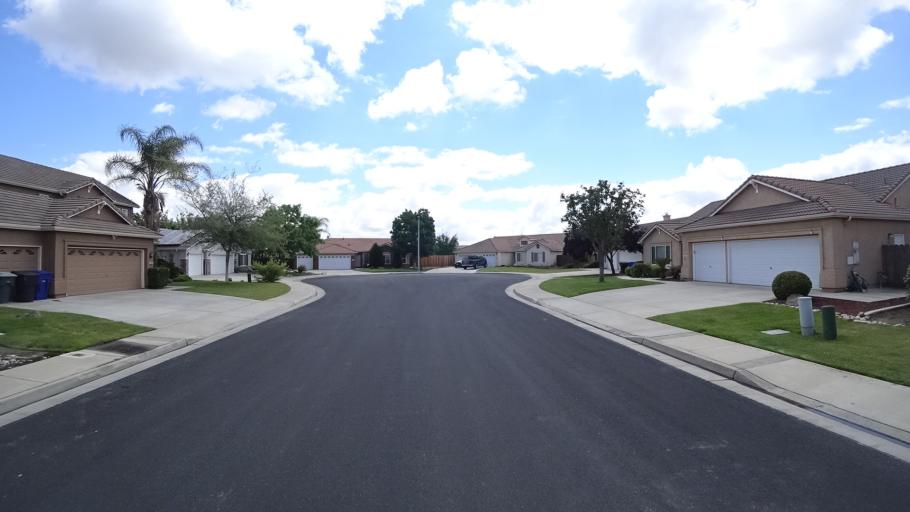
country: US
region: California
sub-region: Kings County
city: Lucerne
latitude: 36.3642
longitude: -119.6613
